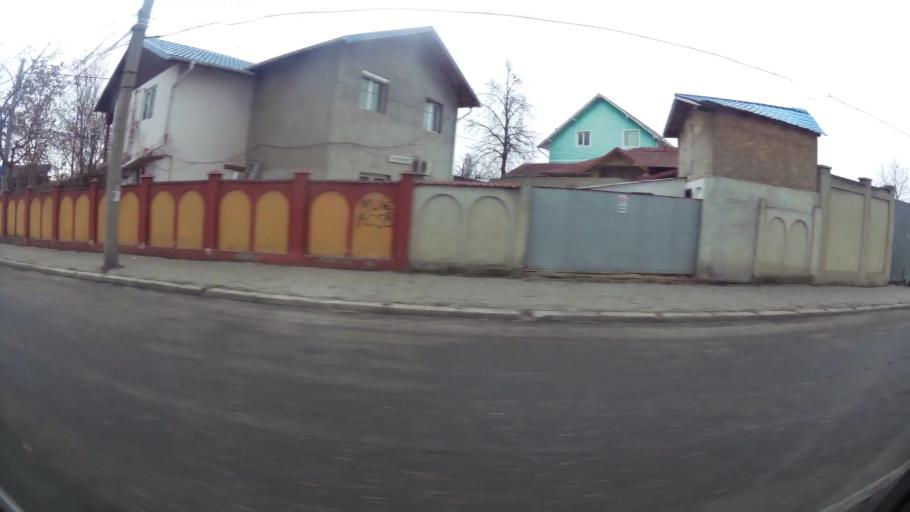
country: RO
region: Prahova
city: Ploiesti
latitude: 44.9453
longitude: 26.0418
